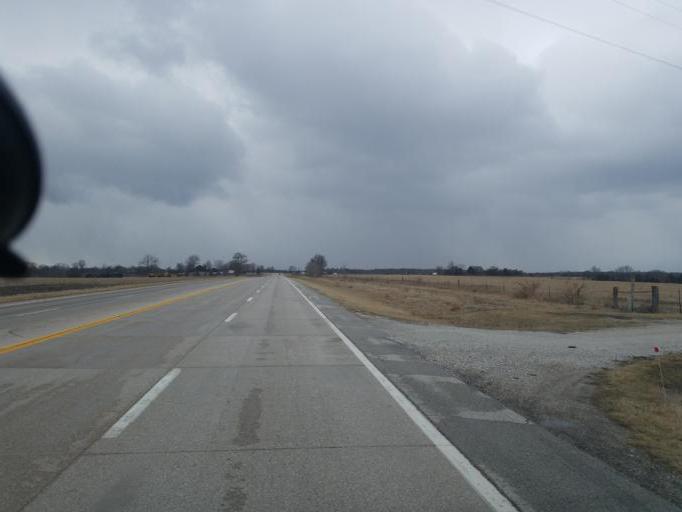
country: US
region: Missouri
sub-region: Macon County
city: Macon
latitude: 39.7955
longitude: -92.4772
